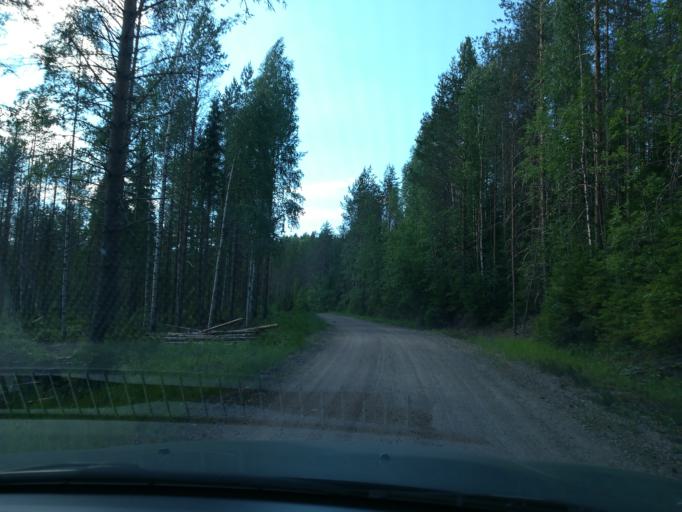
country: FI
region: South Karelia
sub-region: Imatra
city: Ruokolahti
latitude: 61.5376
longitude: 28.8294
